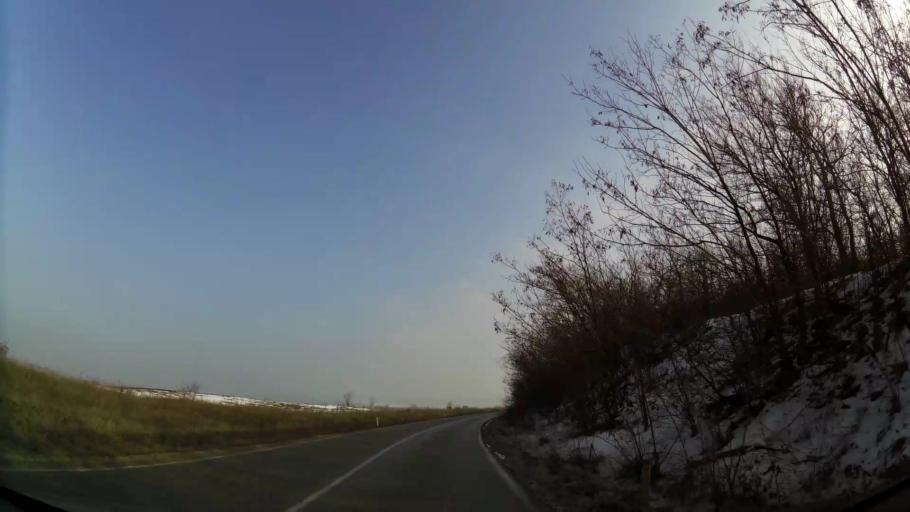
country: MK
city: Miladinovci
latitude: 41.9768
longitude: 21.6294
